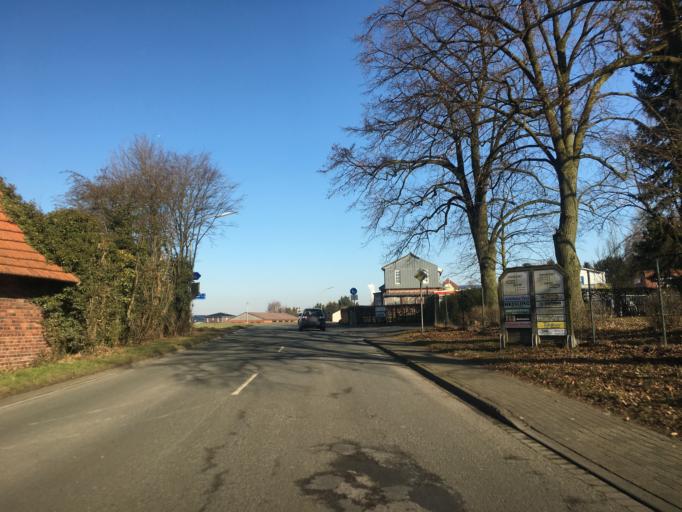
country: DE
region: North Rhine-Westphalia
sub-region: Regierungsbezirk Munster
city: Billerbeck
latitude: 52.0249
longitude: 7.2761
